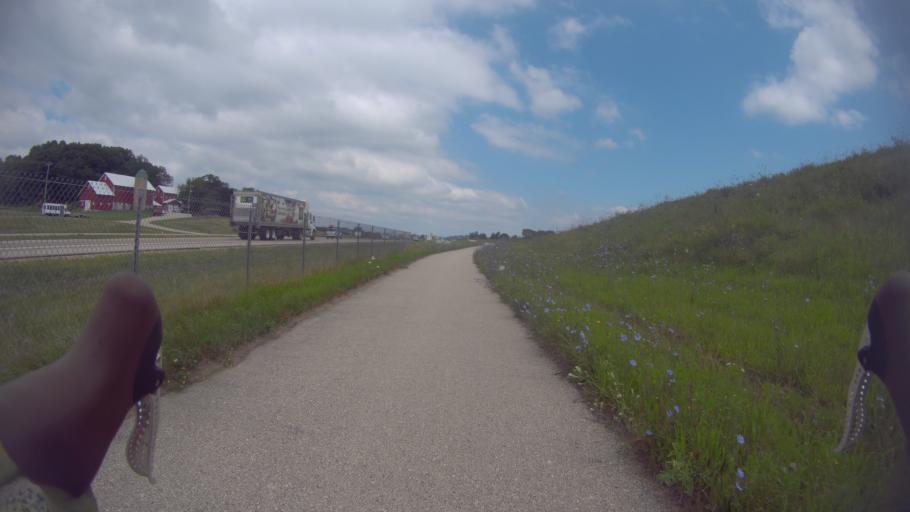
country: US
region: Wisconsin
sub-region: Dane County
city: Middleton
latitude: 43.1364
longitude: -89.5173
